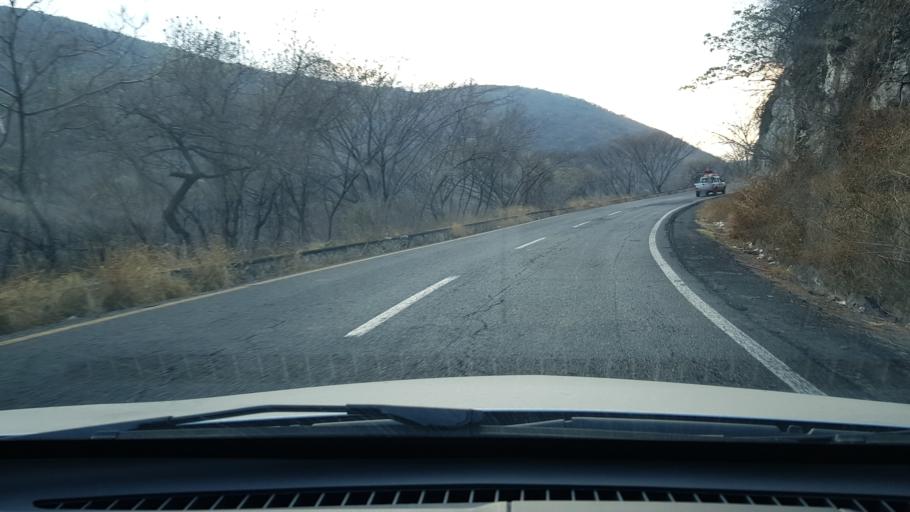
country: MX
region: Morelos
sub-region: Jiutepec
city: Independencia
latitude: 18.8607
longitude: -99.1194
